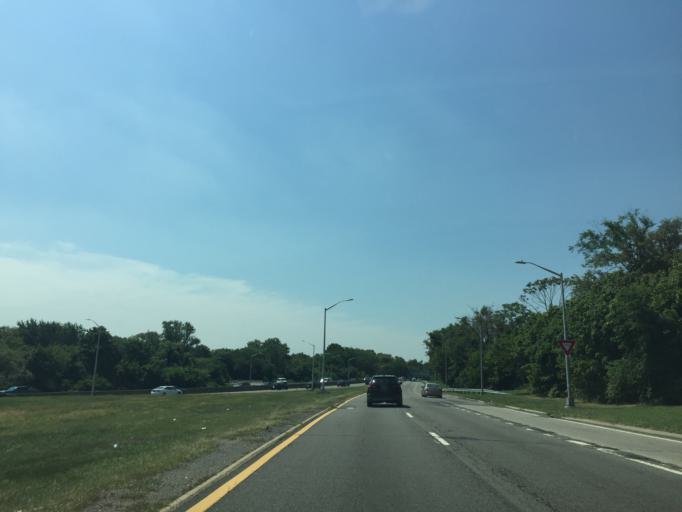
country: US
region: New York
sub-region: Nassau County
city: Elmont
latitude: 40.6872
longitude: -73.7263
